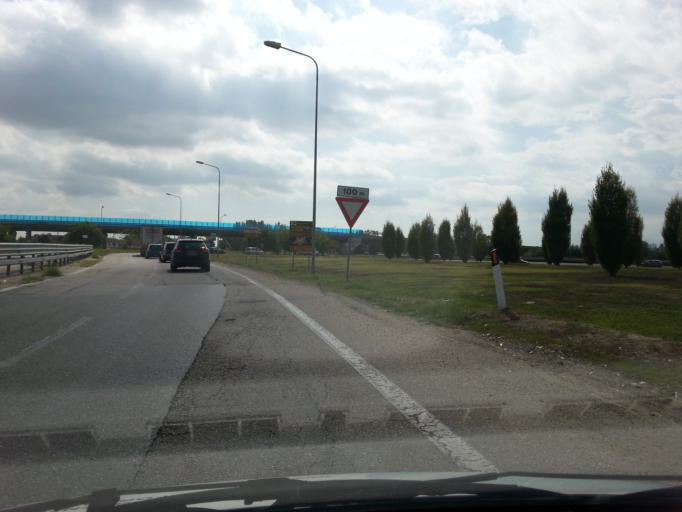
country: IT
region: Piedmont
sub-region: Provincia di Torino
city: Pinerolo
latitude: 44.8816
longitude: 7.3551
